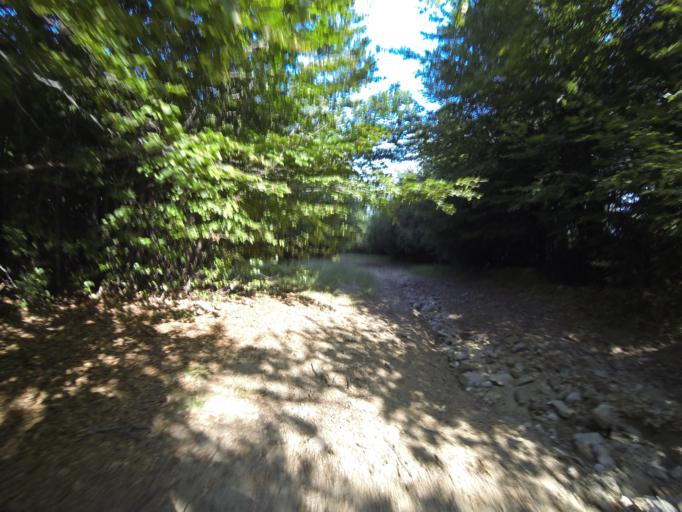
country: RO
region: Valcea
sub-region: Comuna Vaideeni
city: Vaideeni
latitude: 45.2339
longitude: 23.9619
